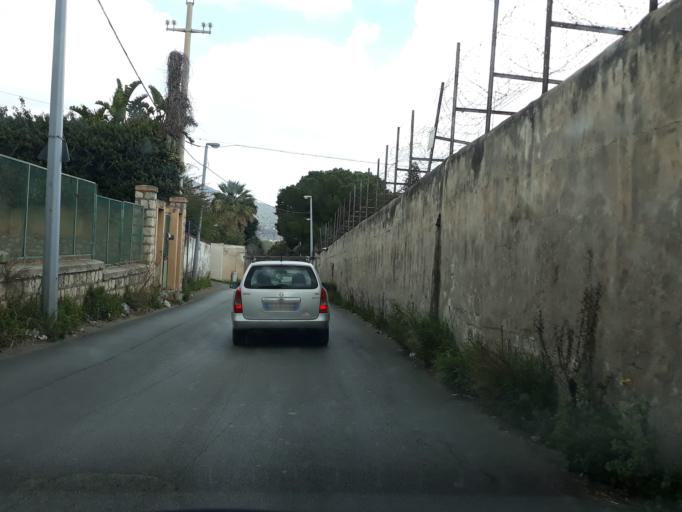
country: IT
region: Sicily
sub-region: Palermo
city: Palermo
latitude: 38.1104
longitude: 13.3087
